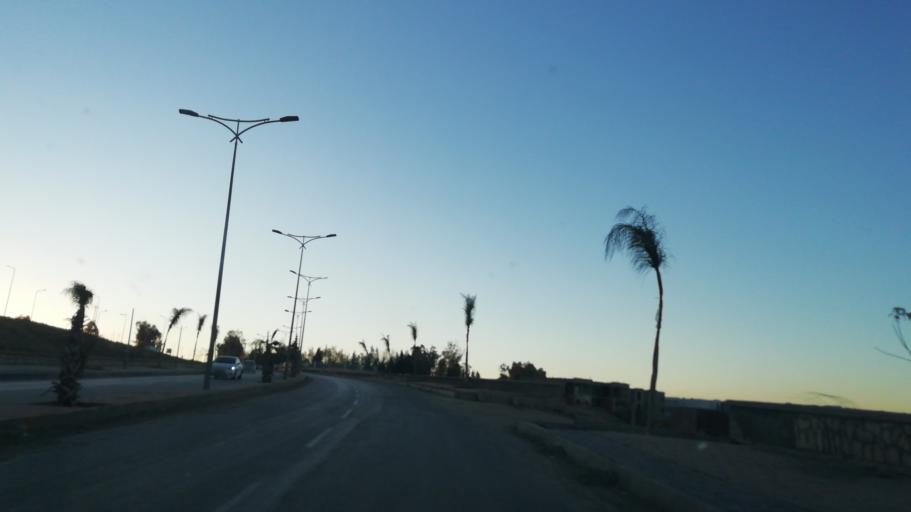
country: DZ
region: Saida
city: Saida
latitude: 34.8350
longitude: 0.1739
